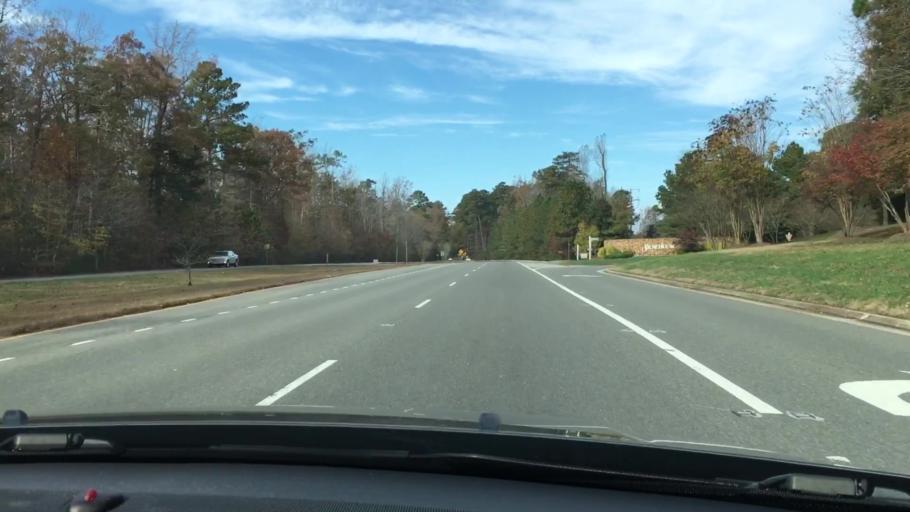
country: US
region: Virginia
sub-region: King William County
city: West Point
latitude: 37.4275
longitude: -76.8286
